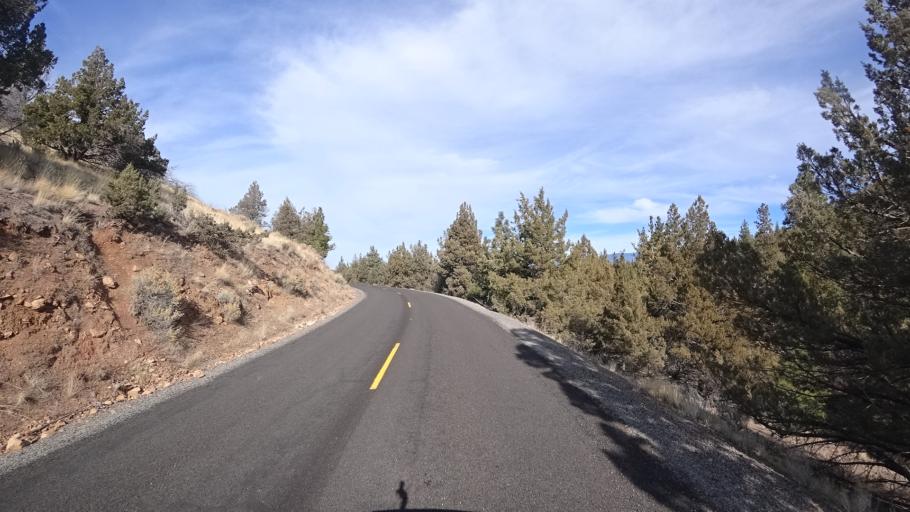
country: US
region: California
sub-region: Siskiyou County
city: Weed
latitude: 41.5001
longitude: -122.3898
